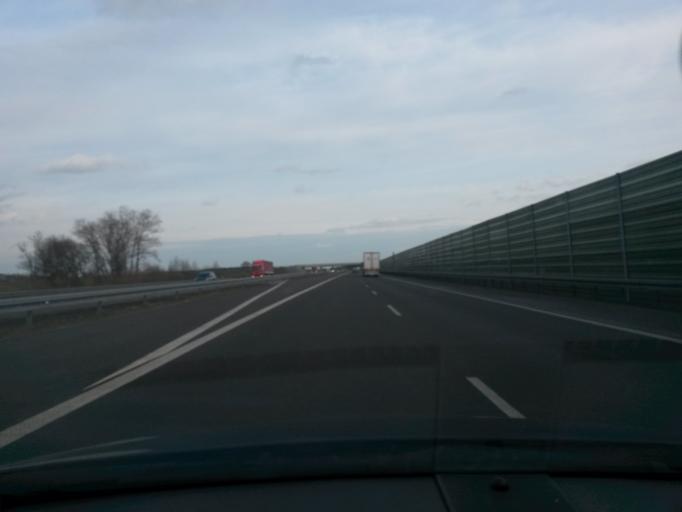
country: PL
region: Greater Poland Voivodeship
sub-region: Powiat kolski
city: Dabie
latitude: 52.1089
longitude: 18.7459
